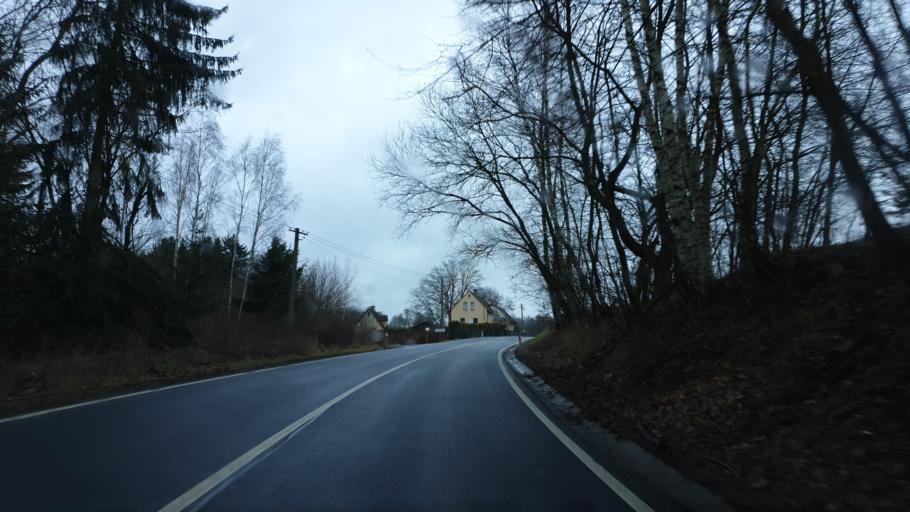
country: CZ
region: Karlovarsky
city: As
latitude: 50.2441
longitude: 12.1828
